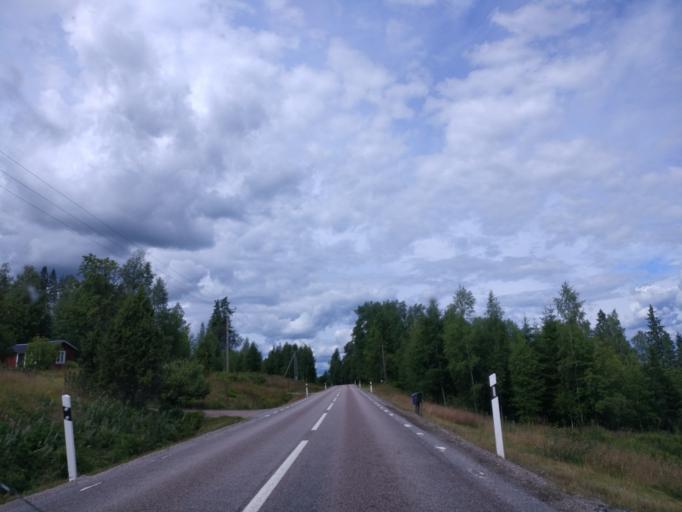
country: SE
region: Vaermland
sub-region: Hagfors Kommun
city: Ekshaerad
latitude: 60.1850
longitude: 13.3413
